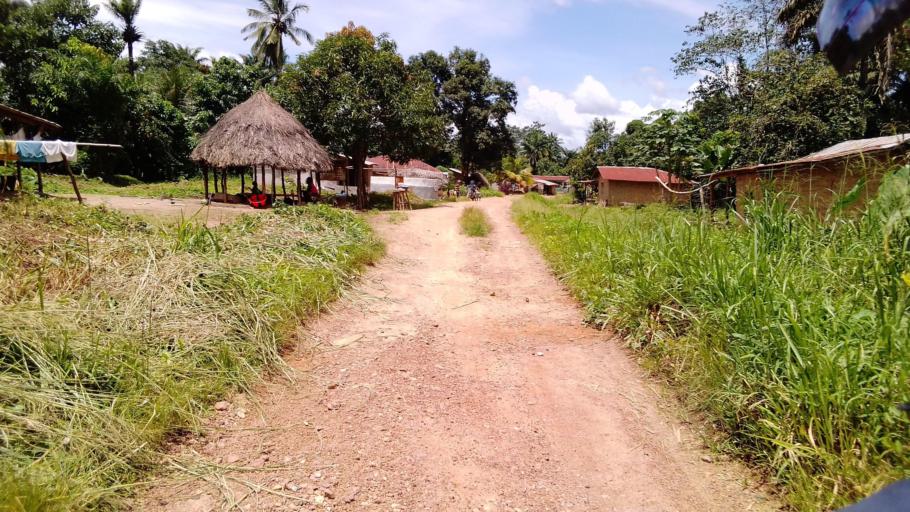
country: SL
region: Eastern Province
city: Koidu
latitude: 8.6975
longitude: -10.9537
